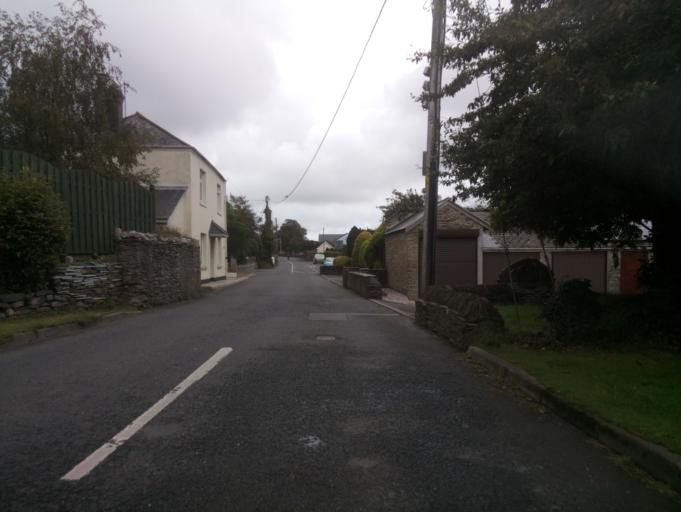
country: GB
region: England
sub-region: Devon
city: Kingsbridge
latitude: 50.2728
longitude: -3.7020
